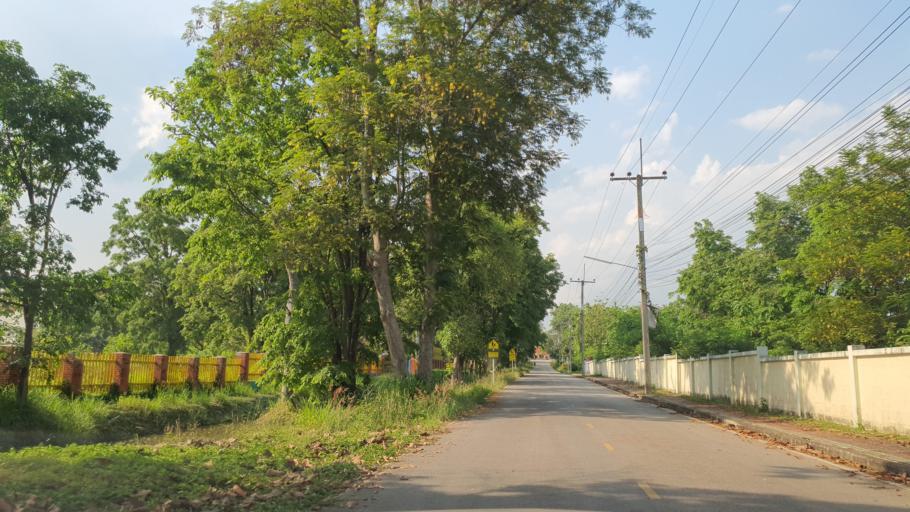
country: TH
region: Chiang Mai
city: San Pa Tong
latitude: 18.6461
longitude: 98.8476
